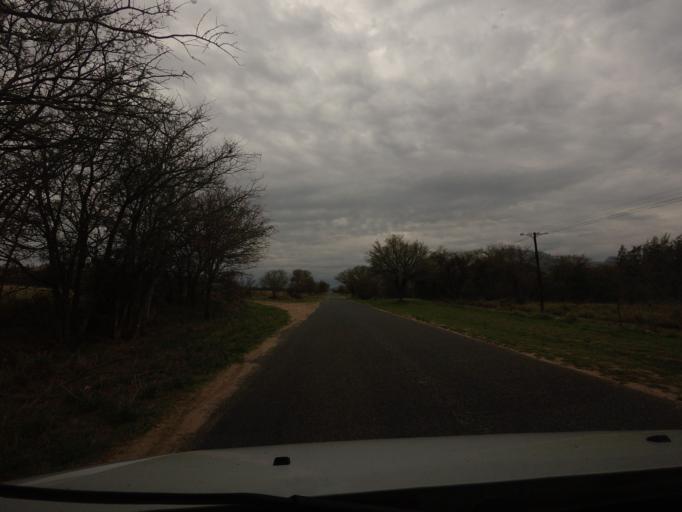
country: ZA
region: Limpopo
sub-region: Mopani District Municipality
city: Hoedspruit
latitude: -24.4538
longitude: 30.8640
